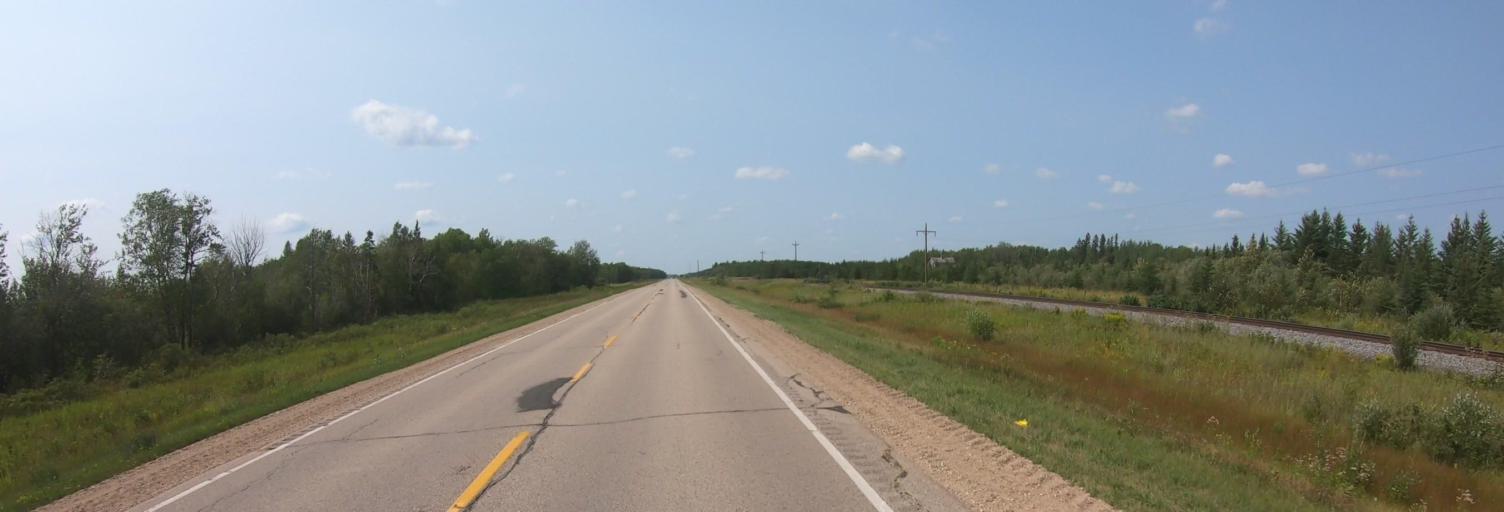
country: US
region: Minnesota
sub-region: Lake of the Woods County
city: Baudette
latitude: 48.7542
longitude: -94.8974
